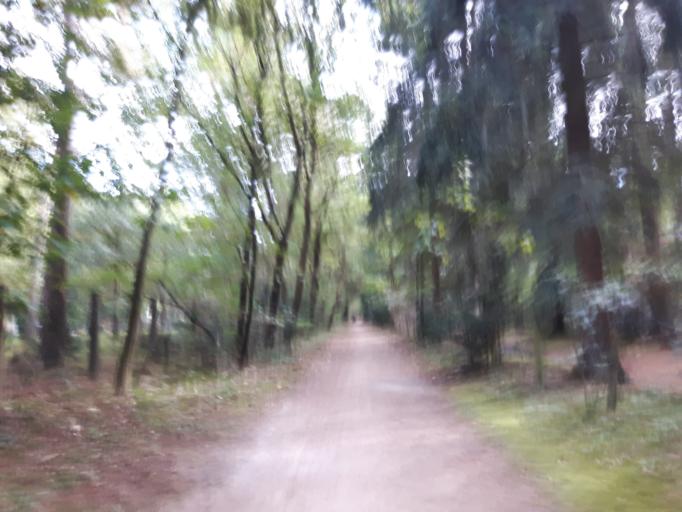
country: NL
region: Utrecht
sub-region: Gemeente Utrechtse Heuvelrug
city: Driebergen-Rijsenburg
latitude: 52.0637
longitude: 5.3045
